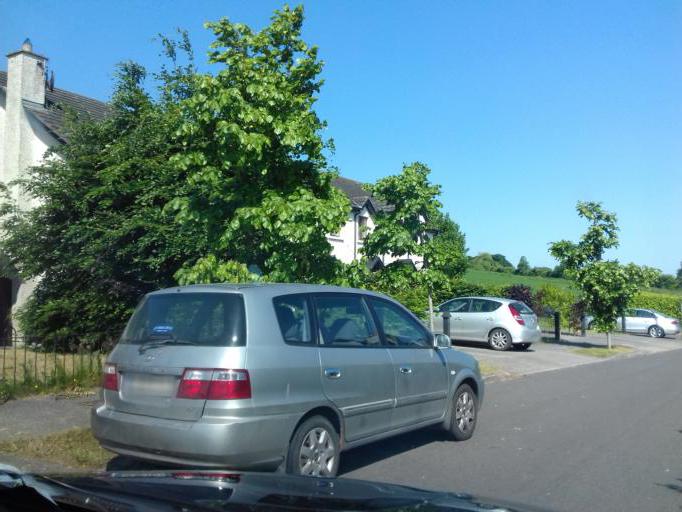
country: IE
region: Leinster
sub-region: An Mhi
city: Slane
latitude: 53.7129
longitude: -6.5515
